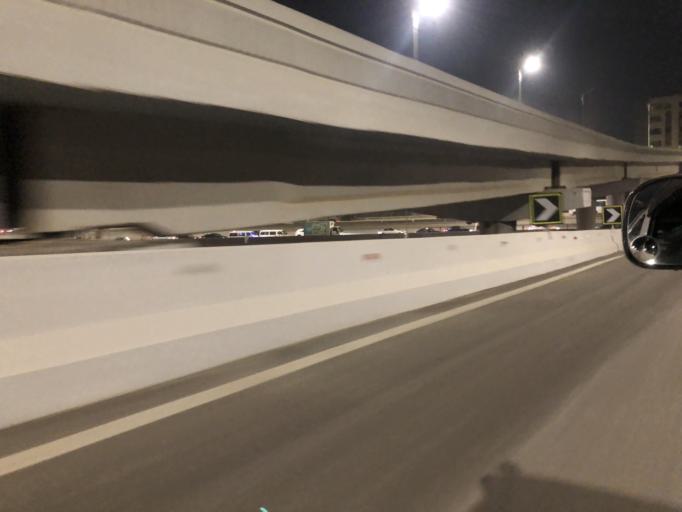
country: EG
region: Al Jizah
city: Al Jizah
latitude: 29.9910
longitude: 31.2599
